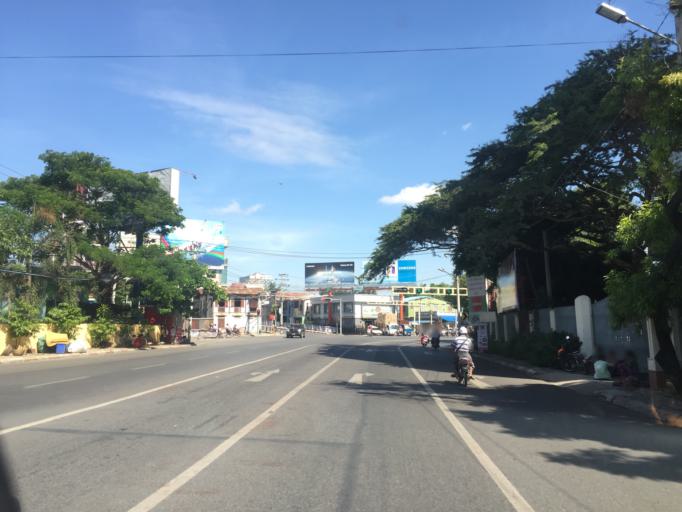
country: MM
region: Mandalay
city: Mandalay
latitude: 21.9583
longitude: 96.0865
